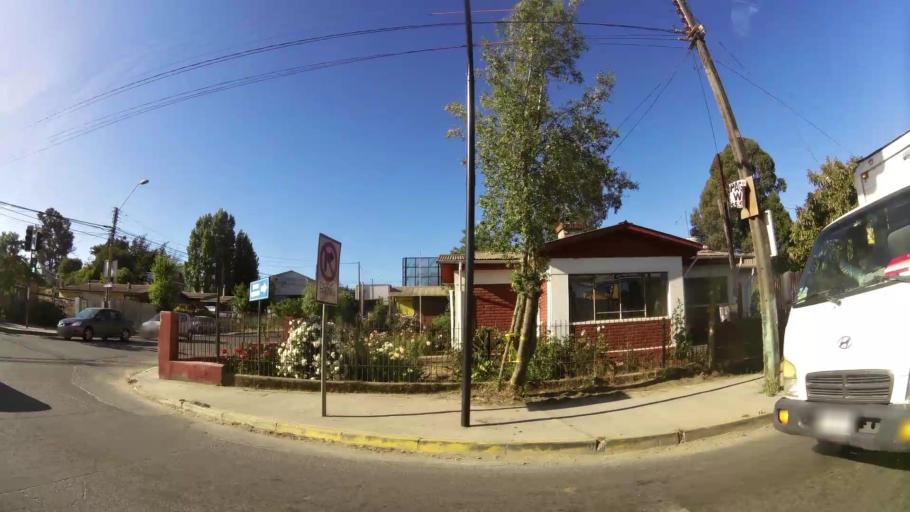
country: CL
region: Valparaiso
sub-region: Provincia de Valparaiso
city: Vina del Mar
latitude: -33.1160
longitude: -71.5615
